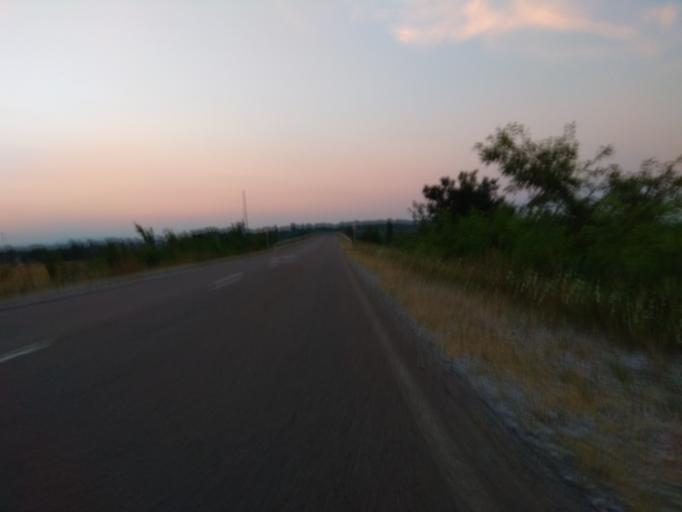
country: HU
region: Borsod-Abauj-Zemplen
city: Emod
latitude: 47.9321
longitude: 20.8298
